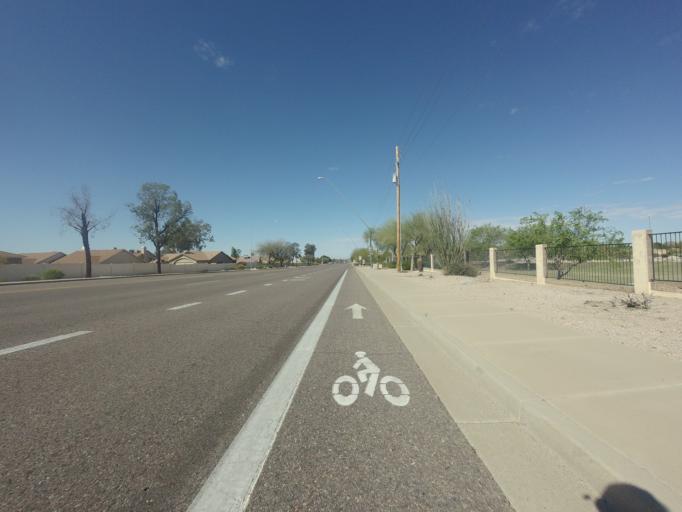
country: US
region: Arizona
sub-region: Maricopa County
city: Mesa
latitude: 33.4665
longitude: -111.6897
